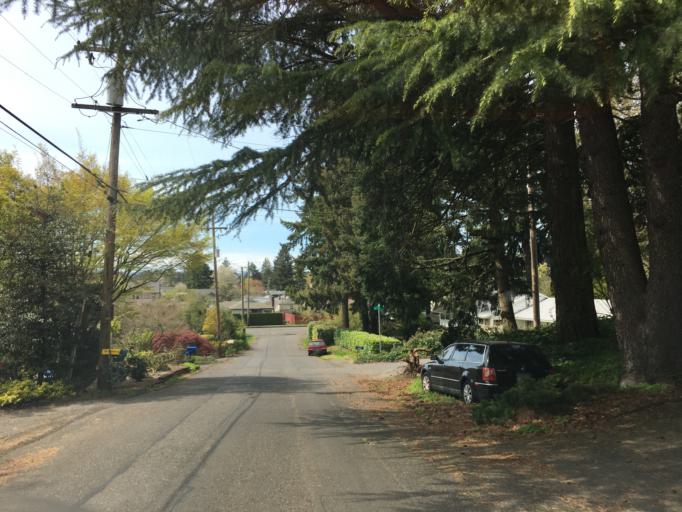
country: US
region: Oregon
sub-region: Multnomah County
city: Lents
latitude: 45.5395
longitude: -122.5671
